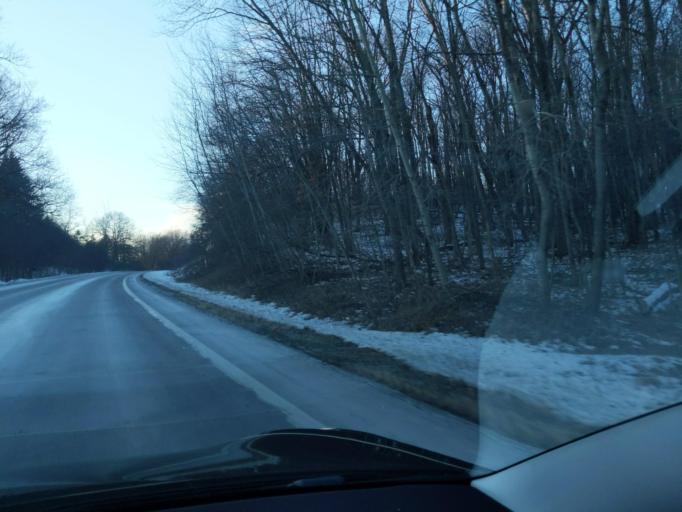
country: US
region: Michigan
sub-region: Ingham County
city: Mason
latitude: 42.5560
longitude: -84.3670
